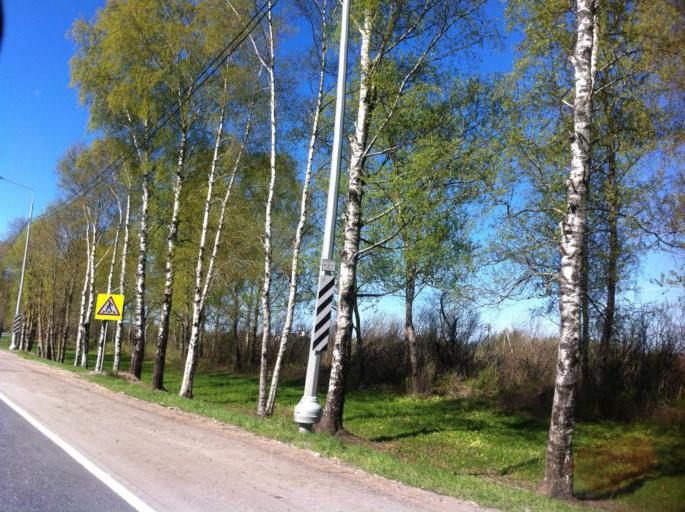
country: RU
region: Pskov
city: Pskov
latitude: 57.7962
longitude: 28.2252
